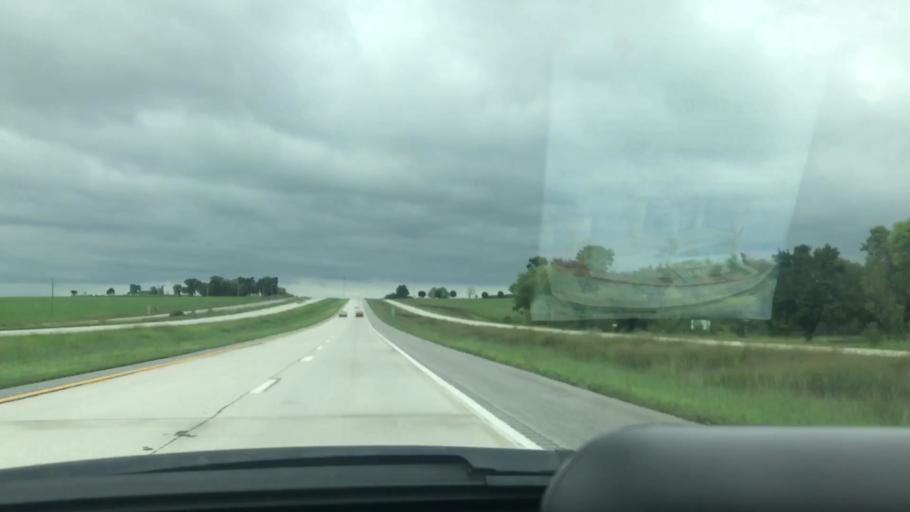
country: US
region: Missouri
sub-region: Greene County
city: Fair Grove
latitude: 37.4300
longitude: -93.1448
